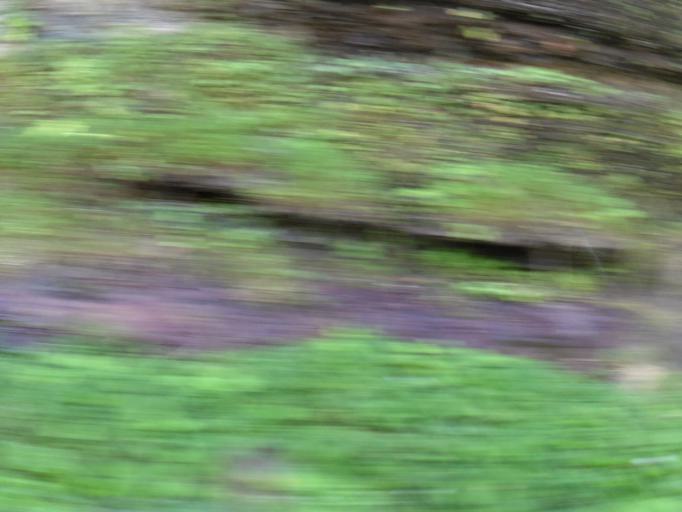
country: US
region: Kentucky
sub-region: Leslie County
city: Hyden
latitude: 37.1626
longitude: -83.5600
